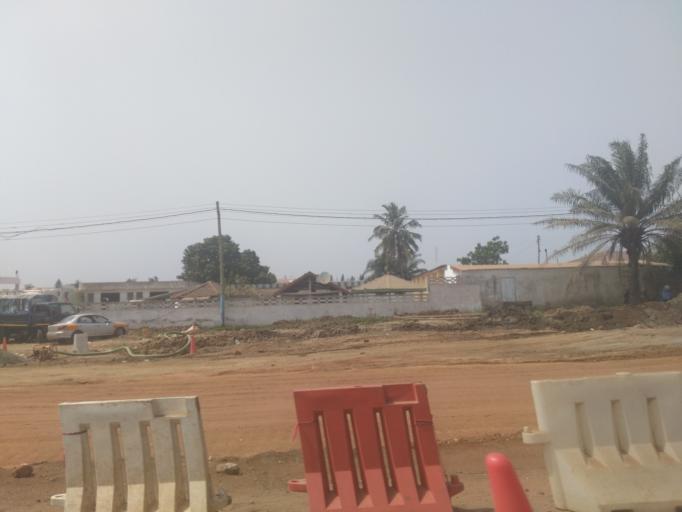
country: GH
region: Greater Accra
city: Tema
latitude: 5.6926
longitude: -0.0133
